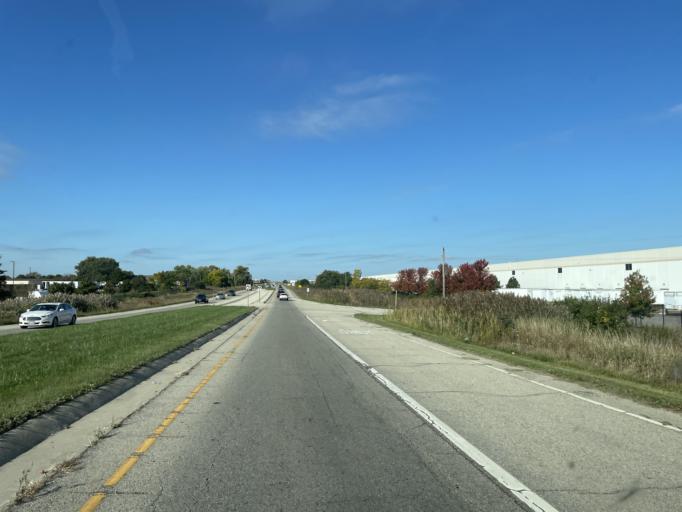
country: US
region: Wisconsin
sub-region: Kenosha County
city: Pleasant Prairie
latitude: 42.5890
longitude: -87.9079
